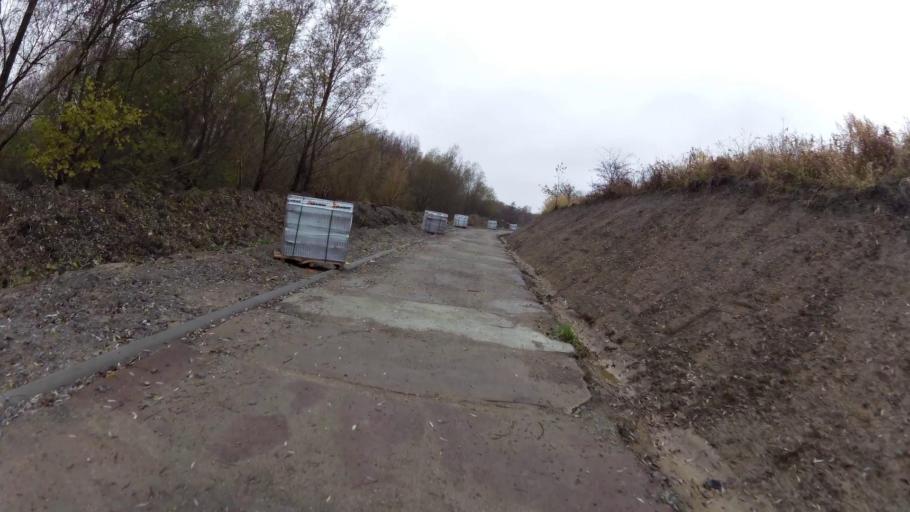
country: PL
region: West Pomeranian Voivodeship
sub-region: Koszalin
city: Koszalin
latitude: 54.2130
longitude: 16.1681
